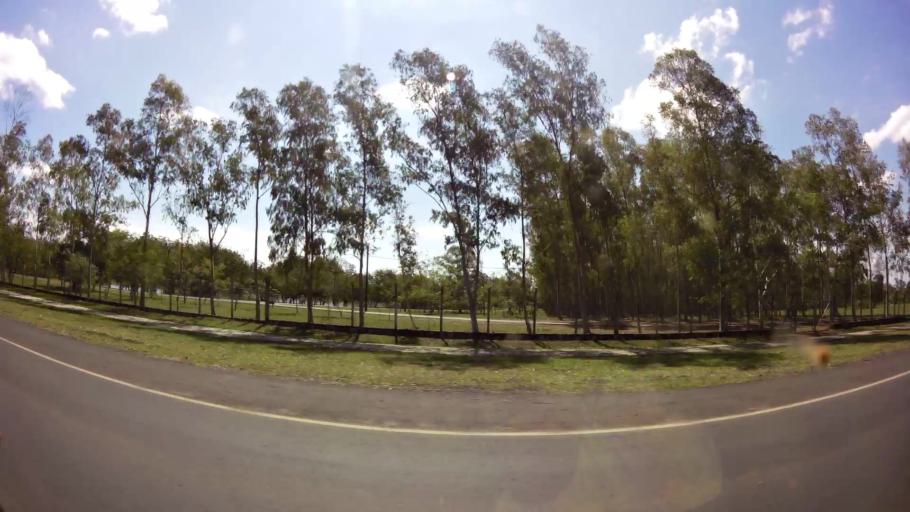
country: PY
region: Central
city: Fernando de la Mora
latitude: -25.2647
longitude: -57.5347
